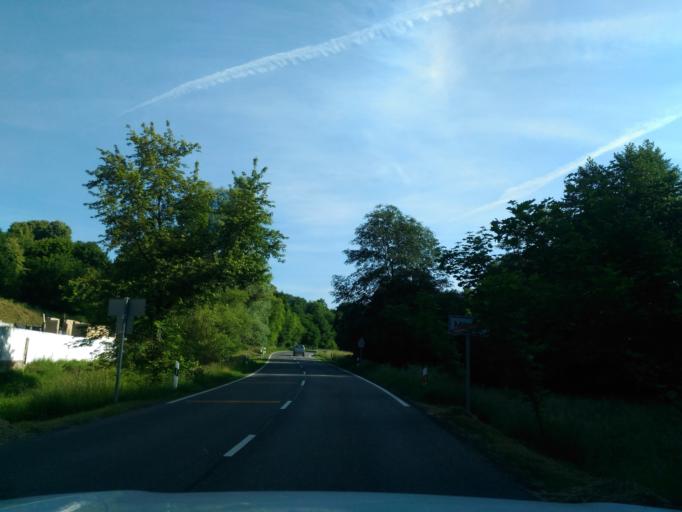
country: HU
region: Baranya
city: Komlo
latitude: 46.1652
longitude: 18.2544
